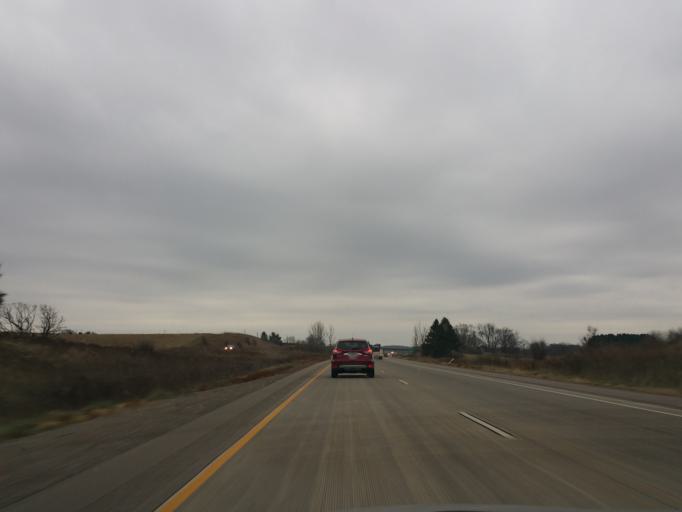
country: US
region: Wisconsin
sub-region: Eau Claire County
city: Fall Creek
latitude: 44.6660
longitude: -91.3176
